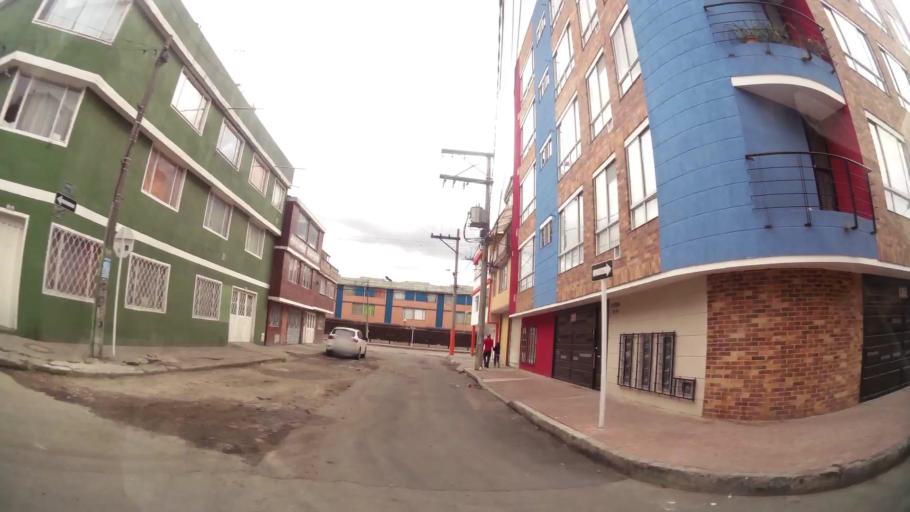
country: CO
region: Bogota D.C.
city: Barrio San Luis
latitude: 4.6990
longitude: -74.1004
